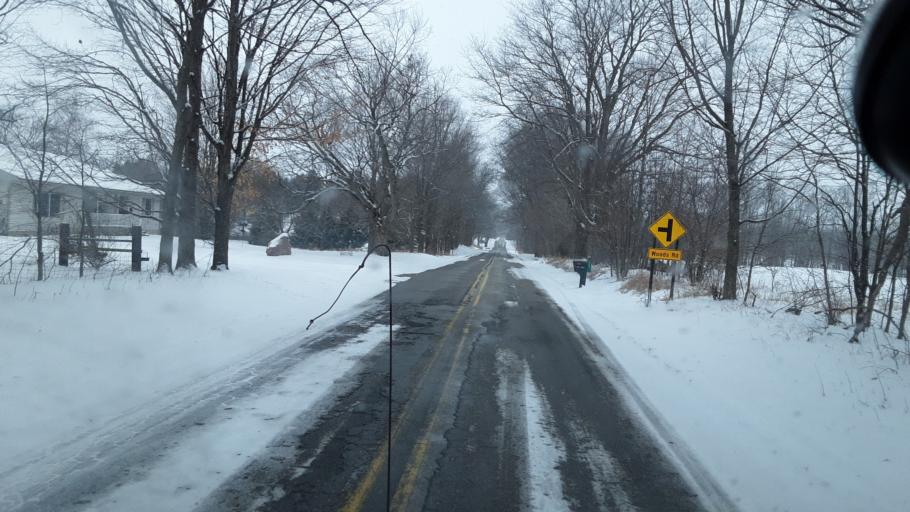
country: US
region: Michigan
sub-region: Ingham County
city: Leslie
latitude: 42.4910
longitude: -84.3766
